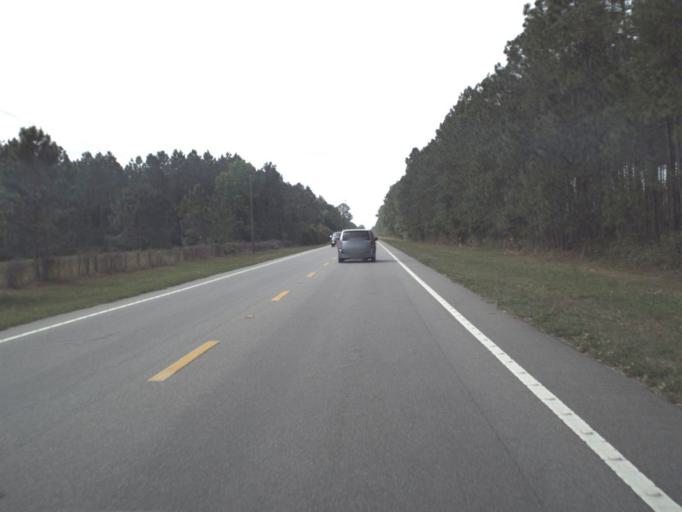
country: US
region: Florida
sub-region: Putnam County
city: Crescent City
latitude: 29.5240
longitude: -81.5091
